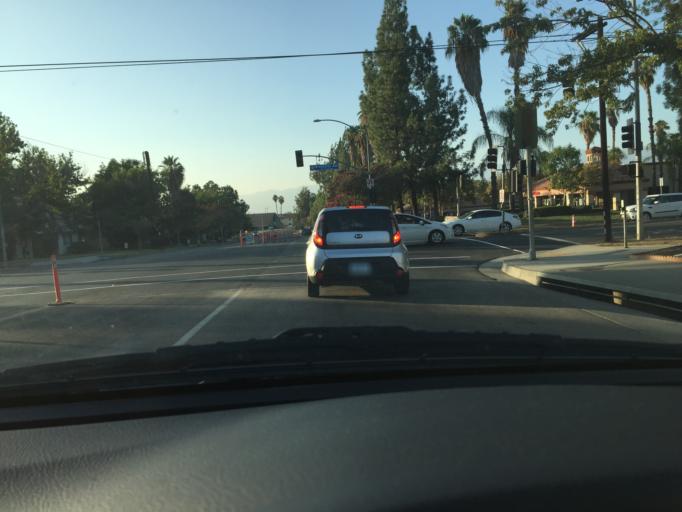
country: US
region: California
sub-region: San Bernardino County
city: Redlands
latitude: 34.0483
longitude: -117.1980
